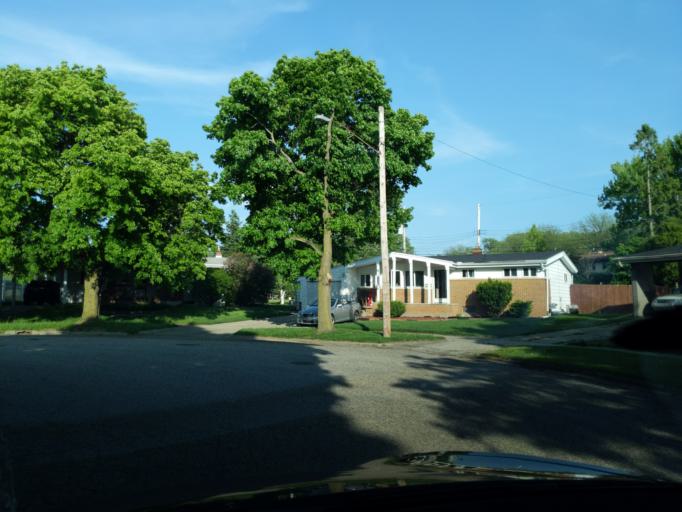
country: US
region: Michigan
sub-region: Ingham County
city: East Lansing
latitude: 42.7492
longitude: -84.5160
